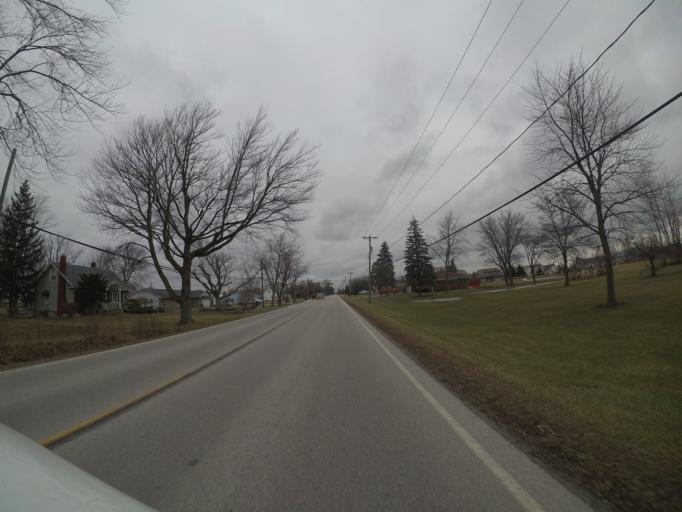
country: US
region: Ohio
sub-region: Wood County
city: Walbridge
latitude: 41.5711
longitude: -83.5121
